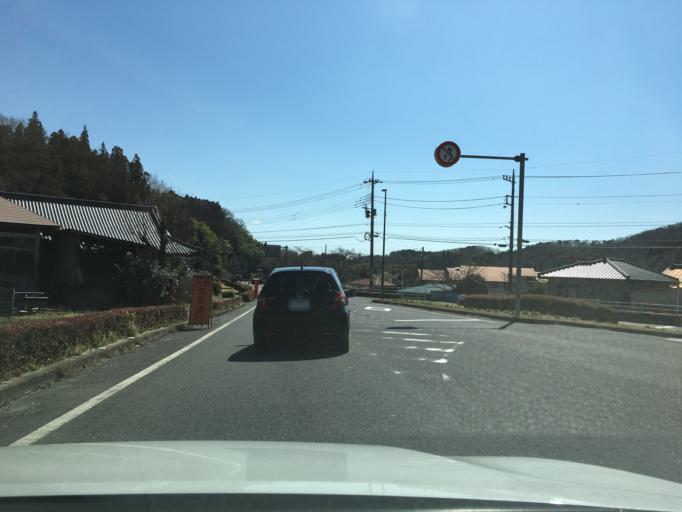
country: JP
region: Tochigi
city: Kuroiso
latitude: 37.0366
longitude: 140.1722
